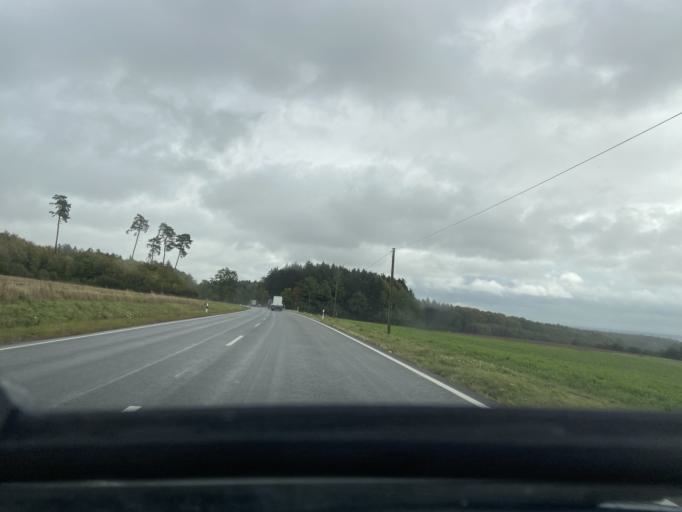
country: DE
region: Baden-Wuerttemberg
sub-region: Freiburg Region
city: Buchheim
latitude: 47.9835
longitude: 9.0449
